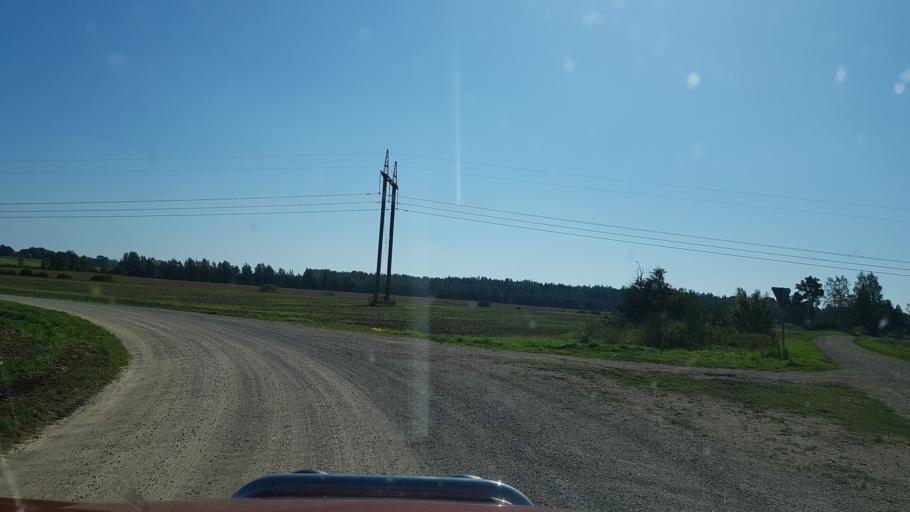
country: EE
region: Tartu
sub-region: UElenurme vald
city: Ulenurme
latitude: 58.2544
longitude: 26.8613
